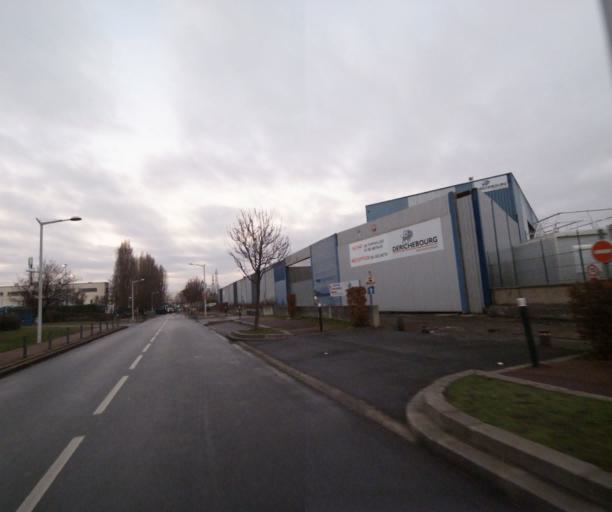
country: FR
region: Ile-de-France
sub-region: Departement des Yvelines
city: Carrieres-sur-Seine
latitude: 48.8961
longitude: 2.1815
